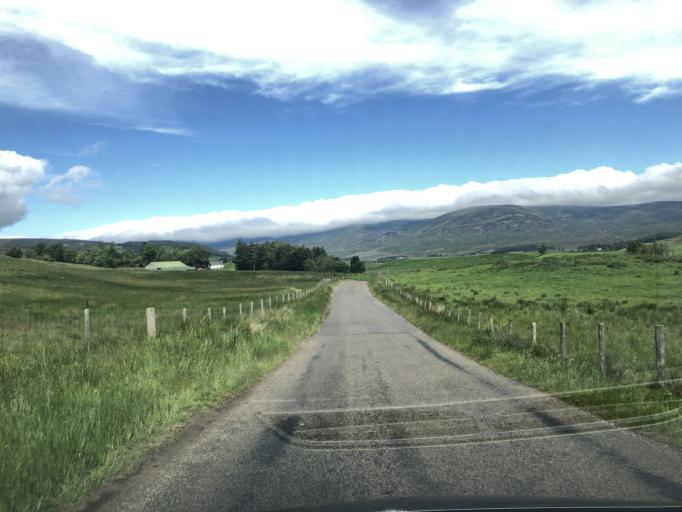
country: GB
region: Scotland
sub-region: Angus
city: Kirriemuir
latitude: 56.7901
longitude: -3.0443
